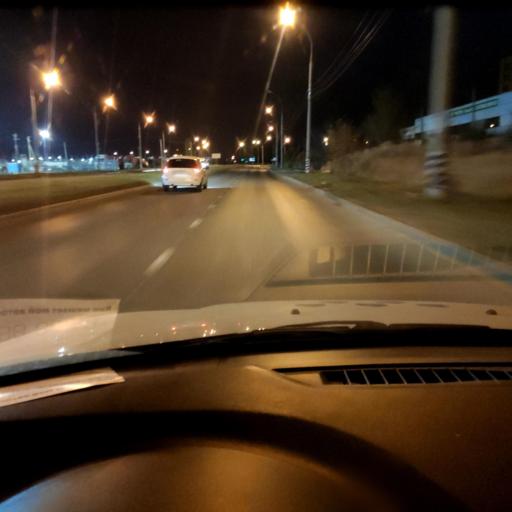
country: RU
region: Samara
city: Tol'yatti
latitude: 53.5565
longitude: 49.3418
